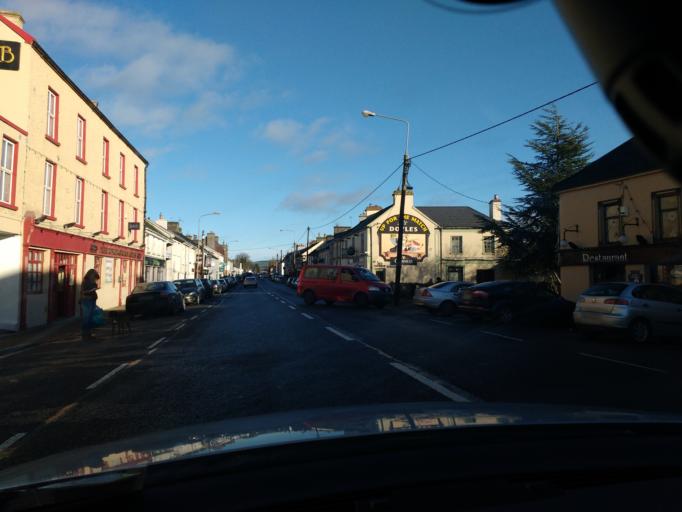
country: IE
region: Leinster
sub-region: Laois
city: Rathdowney
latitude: 52.7196
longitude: -7.5842
